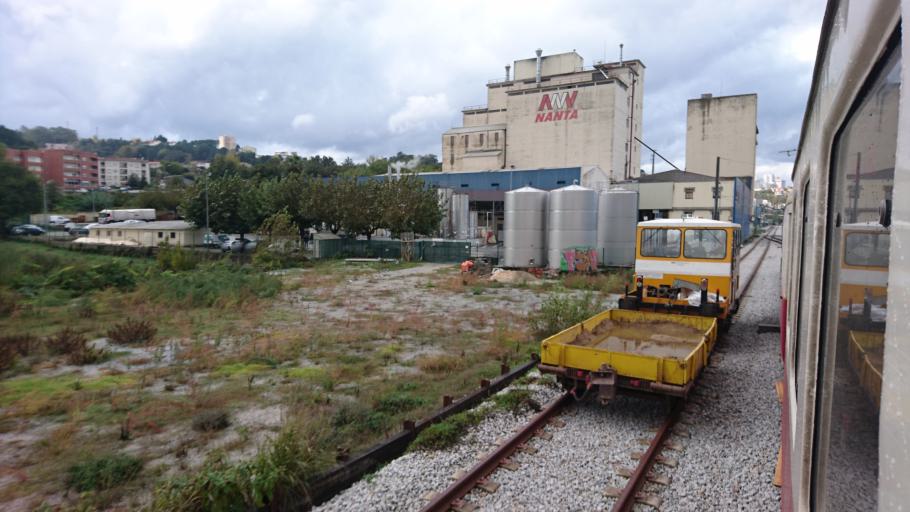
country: PT
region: Porto
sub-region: Marco de Canaveses
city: Marco de Canavezes
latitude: 41.1781
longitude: -8.1345
